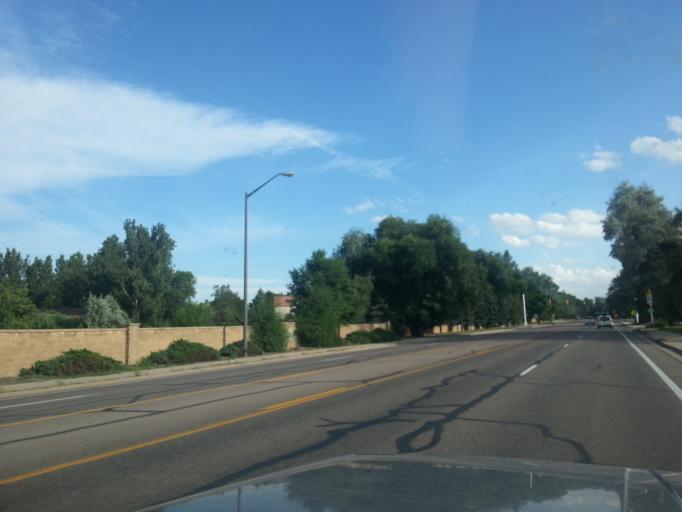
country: US
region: Colorado
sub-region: Larimer County
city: Fort Collins
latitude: 40.5425
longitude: -105.0581
